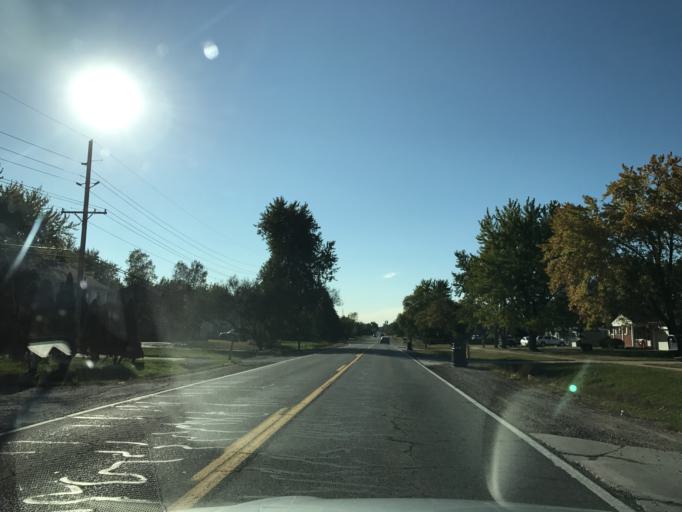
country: US
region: Michigan
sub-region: Oakland County
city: Franklin
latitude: 42.4855
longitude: -83.3237
